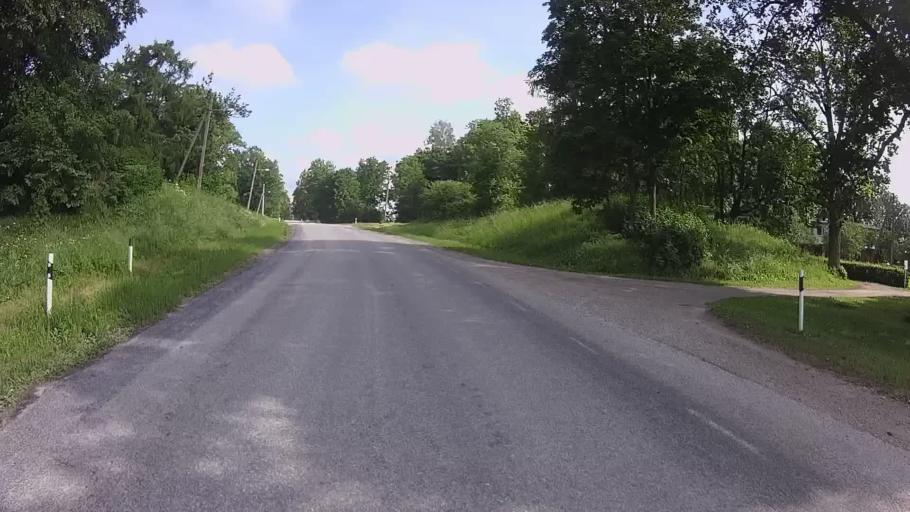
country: EE
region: Vorumaa
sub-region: Antsla vald
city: Vana-Antsla
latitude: 57.8621
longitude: 26.6086
